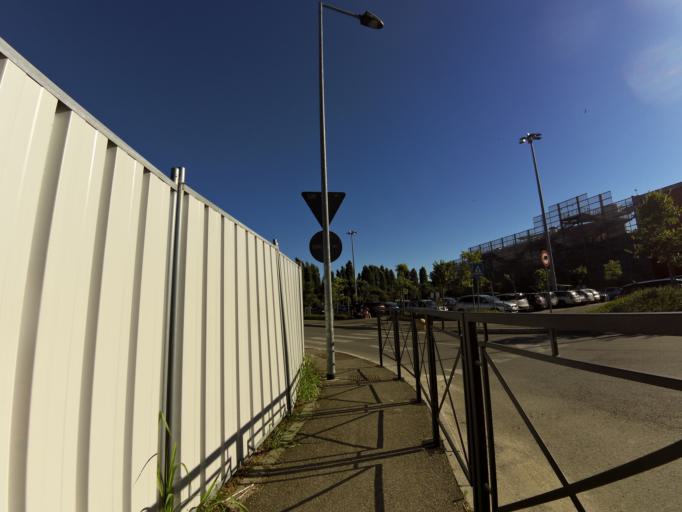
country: IT
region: Lombardy
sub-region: Citta metropolitana di Milano
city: Bettola-Zeloforomagno
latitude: 45.4237
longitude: 9.2961
